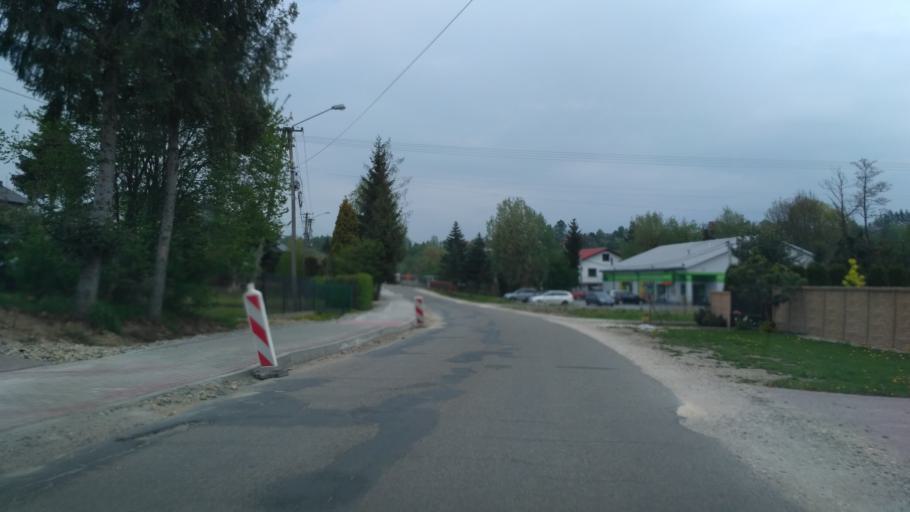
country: PL
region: Lesser Poland Voivodeship
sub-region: Powiat tarnowski
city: Skrzyszow
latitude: 49.9772
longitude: 21.0641
